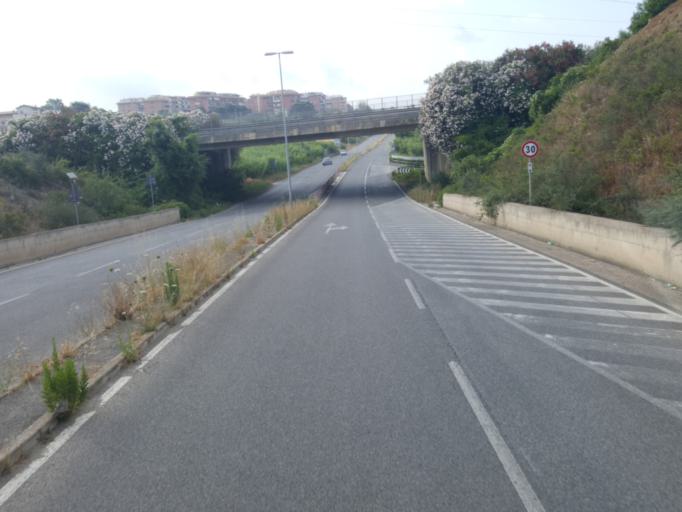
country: IT
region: Latium
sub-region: Citta metropolitana di Roma Capitale
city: Civitavecchia
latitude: 42.1066
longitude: 11.7890
